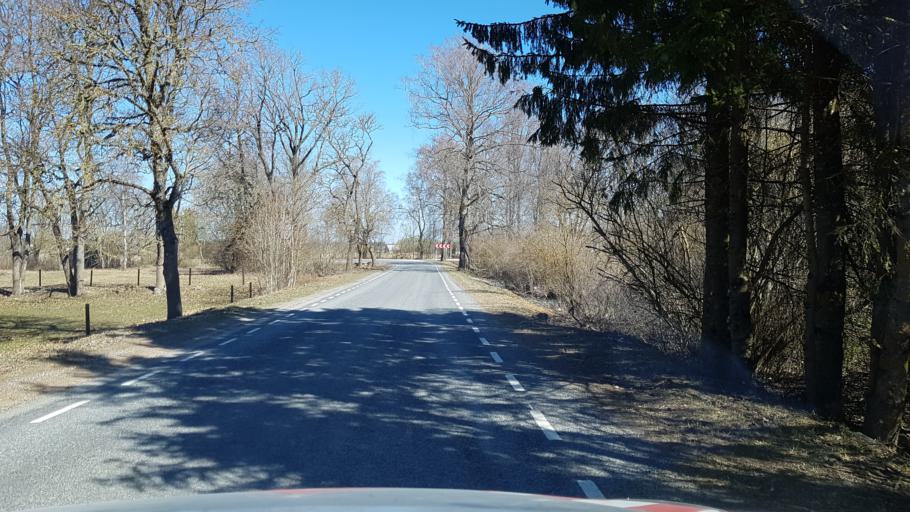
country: EE
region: Laeaene-Virumaa
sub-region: Vinni vald
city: Vinni
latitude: 59.0986
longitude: 26.5247
